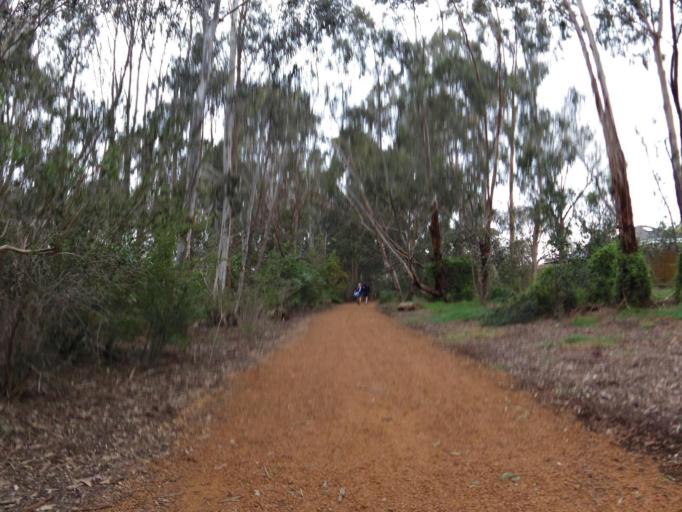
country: AU
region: Victoria
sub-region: Whitehorse
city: Mont Albert North
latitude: -37.7972
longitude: 145.1146
